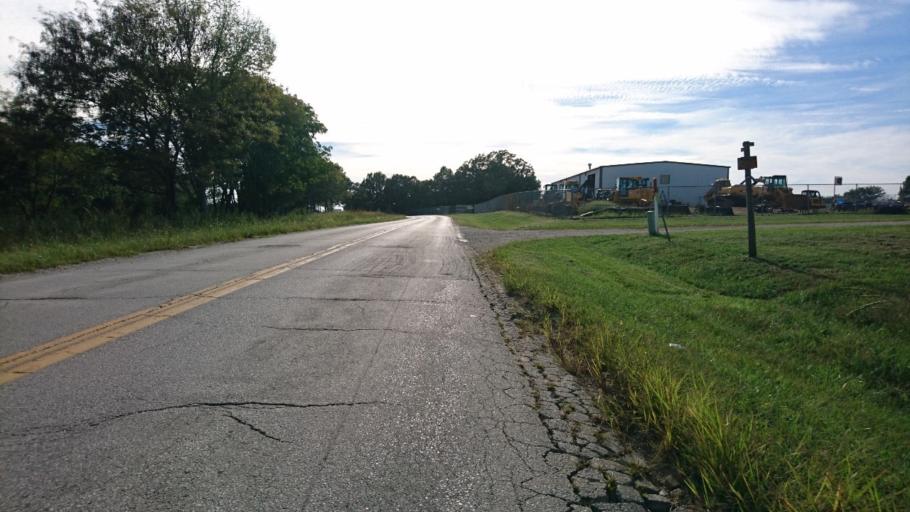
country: US
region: Missouri
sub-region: Crawford County
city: Cuba
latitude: 38.0960
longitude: -91.3617
